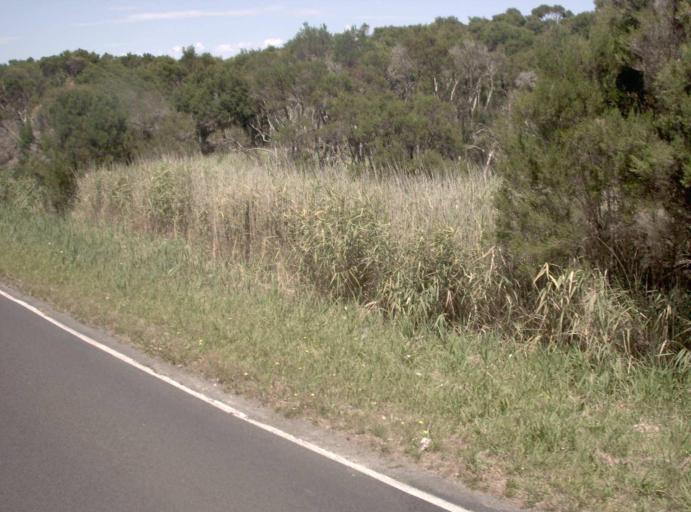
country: AU
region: Victoria
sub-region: Bass Coast
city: North Wonthaggi
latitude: -38.6959
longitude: 145.8785
